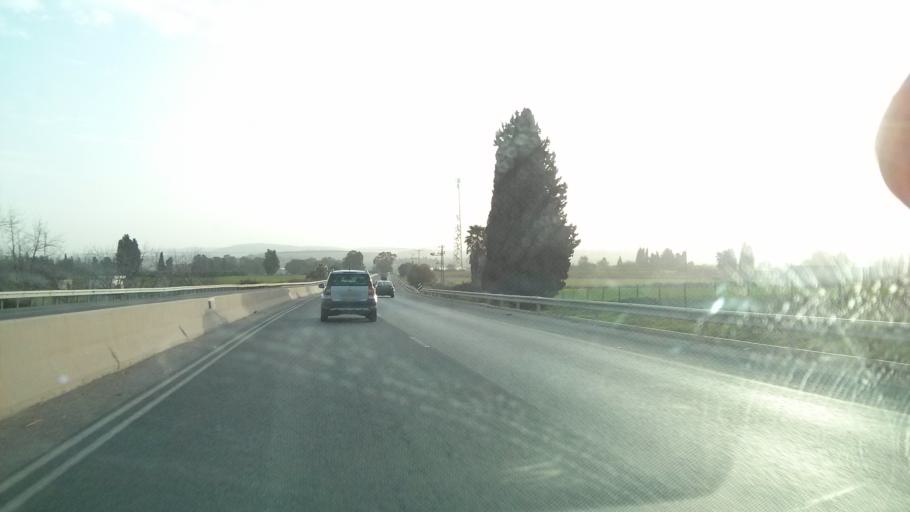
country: PS
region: West Bank
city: Nazlat `Isa
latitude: 32.4693
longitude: 35.0011
